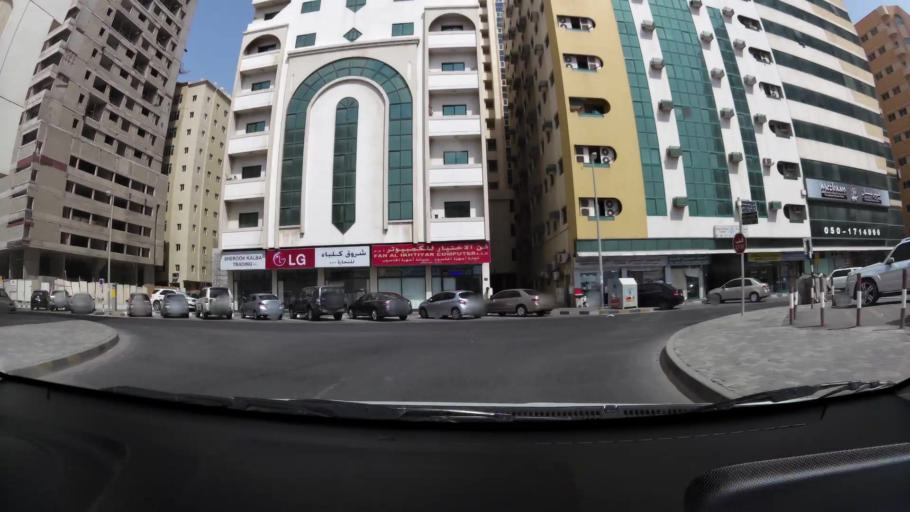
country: AE
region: Ash Shariqah
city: Sharjah
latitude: 25.3481
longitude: 55.3910
